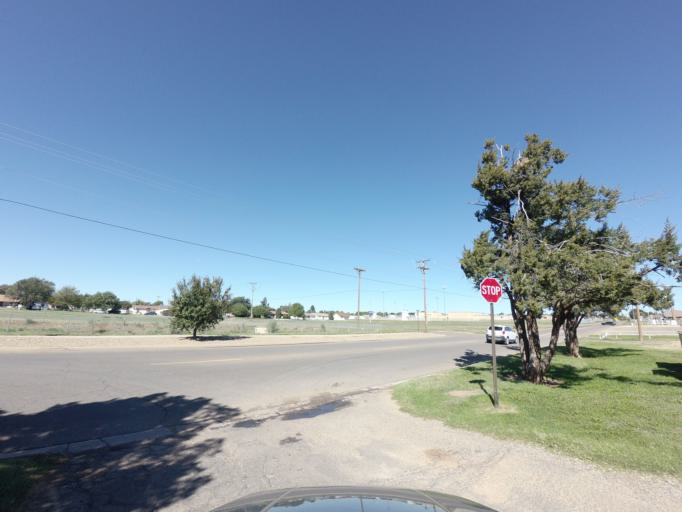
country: US
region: New Mexico
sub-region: Curry County
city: Clovis
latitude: 34.4106
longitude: -103.1876
